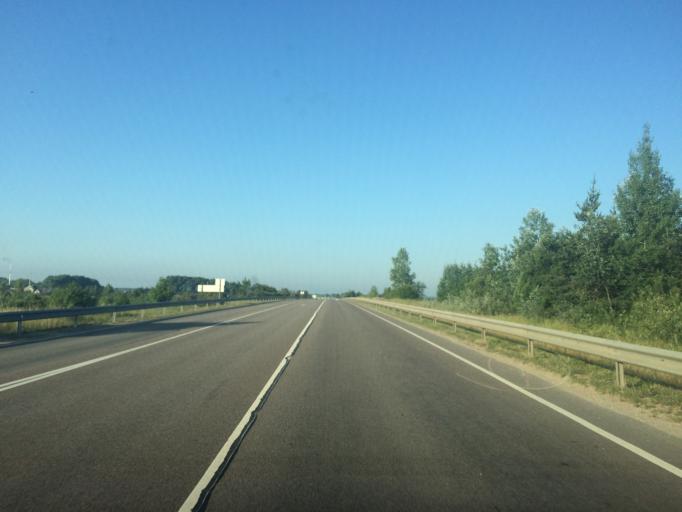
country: LT
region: Vilnius County
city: Ukmerge
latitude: 55.3301
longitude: 24.8847
